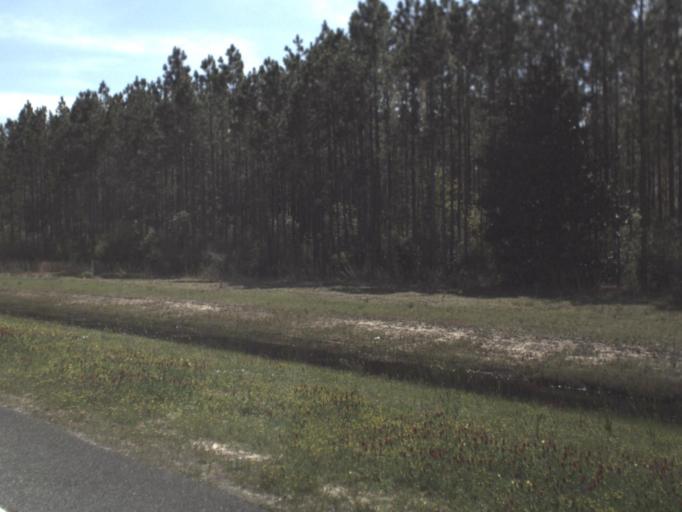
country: US
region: Florida
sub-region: Bay County
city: Lynn Haven
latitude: 30.3427
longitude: -85.6614
